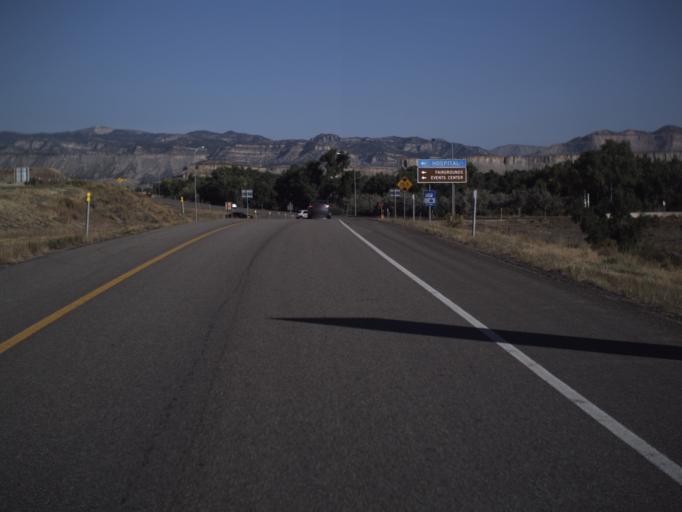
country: US
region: Utah
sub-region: Carbon County
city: Price
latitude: 39.5990
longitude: -110.8255
